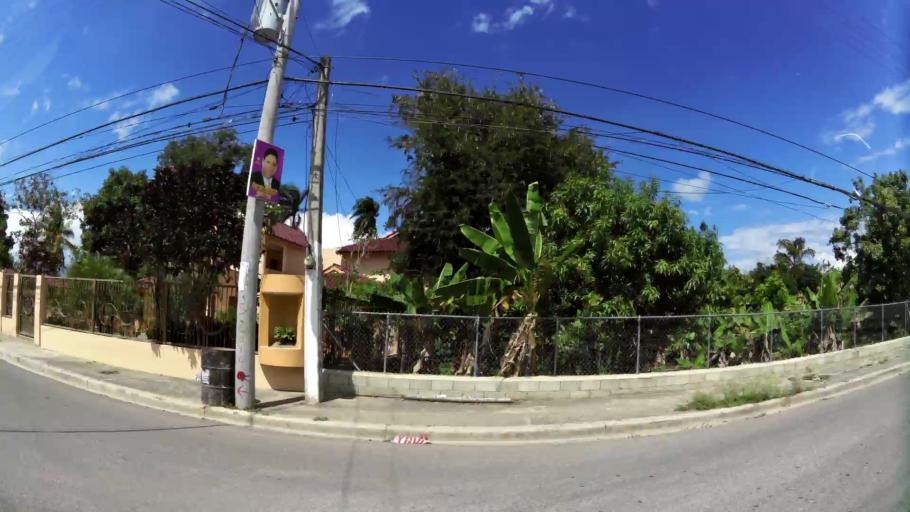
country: DO
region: Santiago
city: Licey al Medio
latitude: 19.3819
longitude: -70.6191
